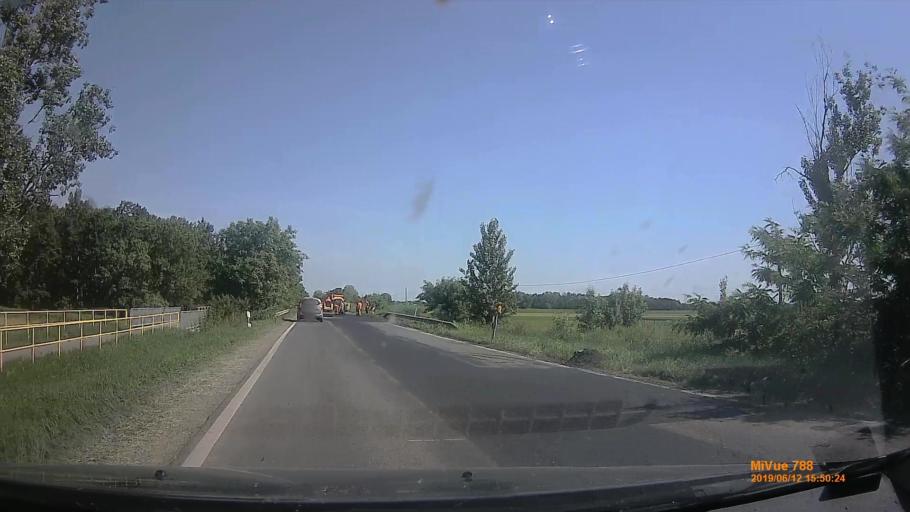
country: HU
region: Csongrad
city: Apatfalva
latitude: 46.1869
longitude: 20.5657
